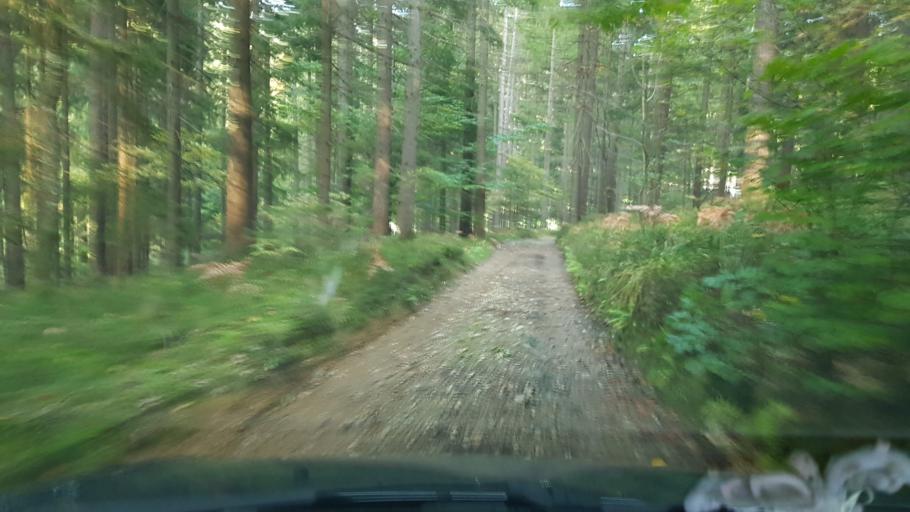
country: SI
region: Slovenj Gradec
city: Smartno pri Slovenj Gradcu
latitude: 46.5100
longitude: 15.1053
